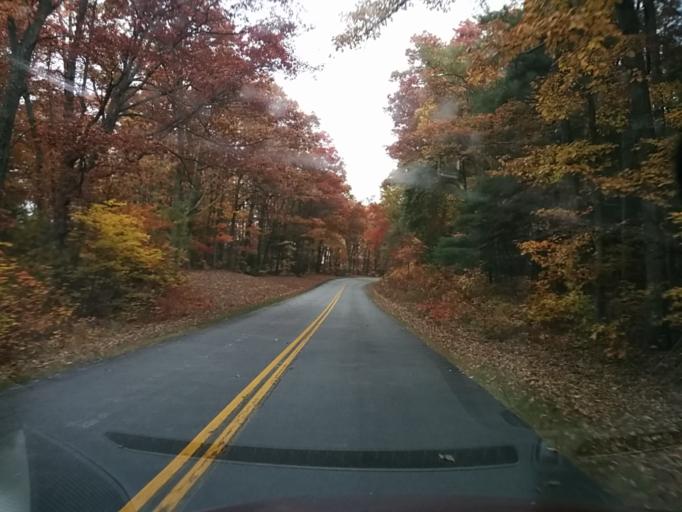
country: US
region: Virginia
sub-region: City of Buena Vista
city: Buena Vista
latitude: 37.7956
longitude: -79.2551
